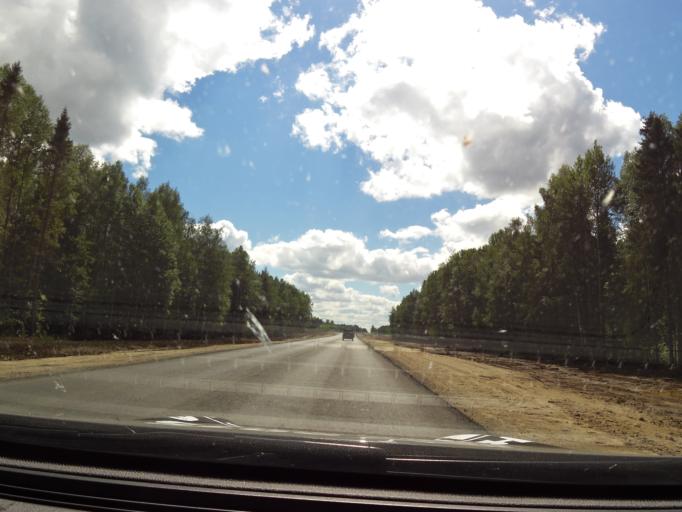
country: RU
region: Vologda
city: Molochnoye
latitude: 59.3482
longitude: 39.6779
